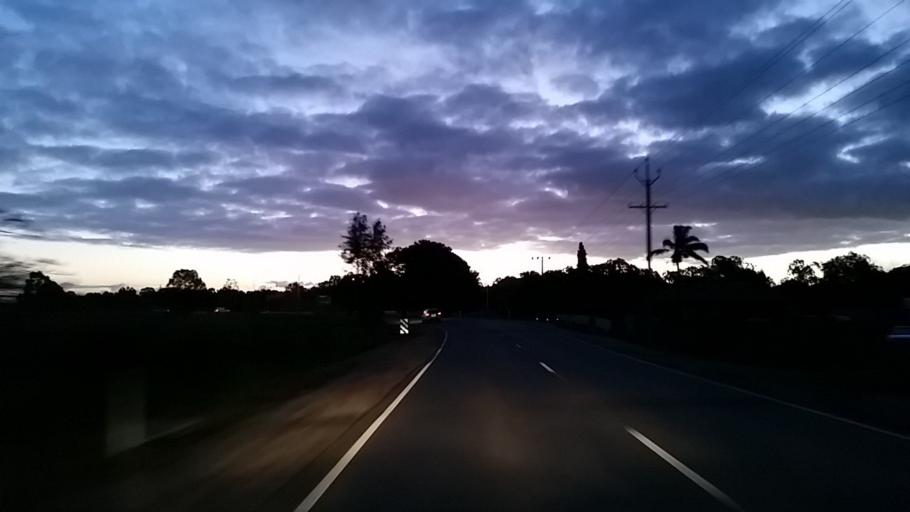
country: AU
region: South Australia
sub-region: Gawler
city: Gawler
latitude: -34.6078
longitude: 138.7326
